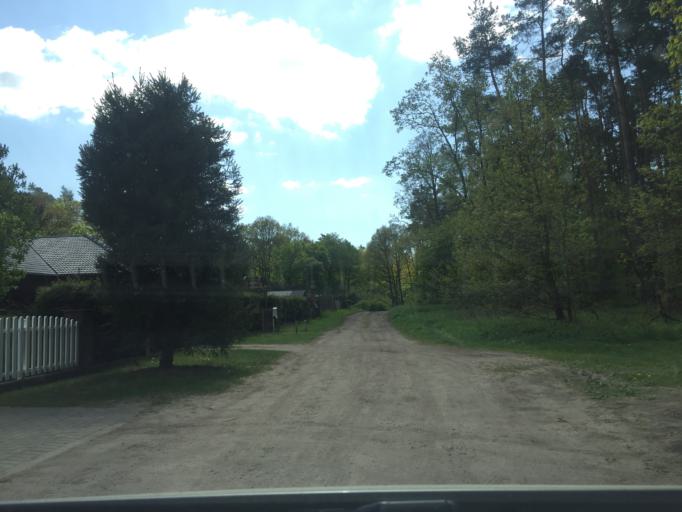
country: DE
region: Mecklenburg-Vorpommern
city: Torgelow
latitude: 53.6205
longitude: 13.9908
